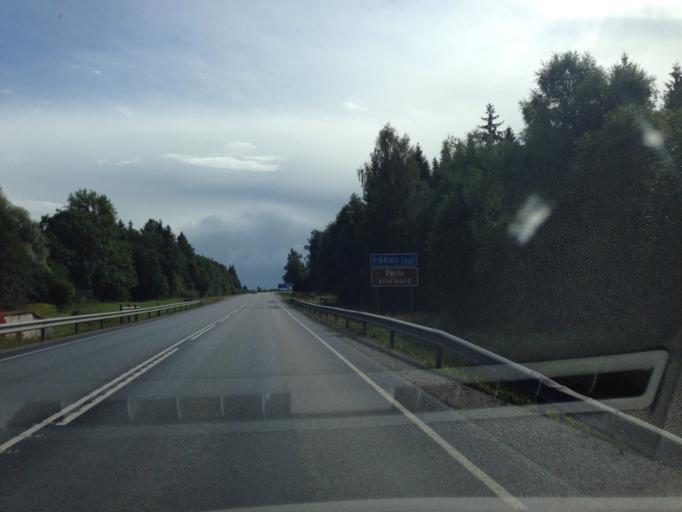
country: EE
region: Jaervamaa
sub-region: Paide linn
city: Paide
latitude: 58.9454
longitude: 25.6114
